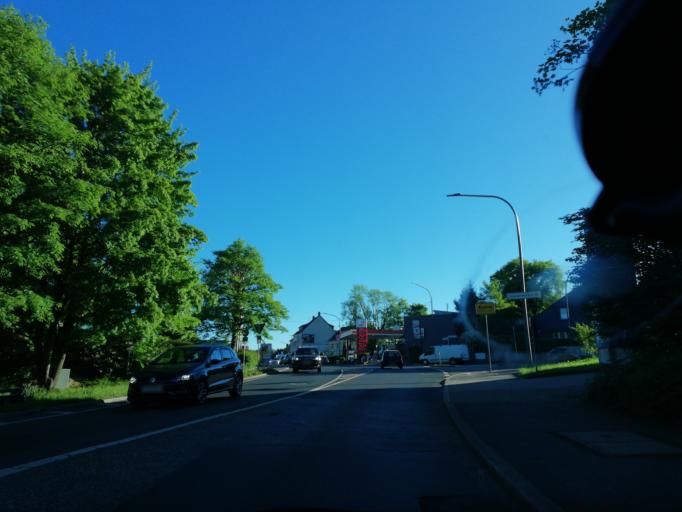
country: DE
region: North Rhine-Westphalia
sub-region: Regierungsbezirk Dusseldorf
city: Wuppertal
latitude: 51.2437
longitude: 7.1908
